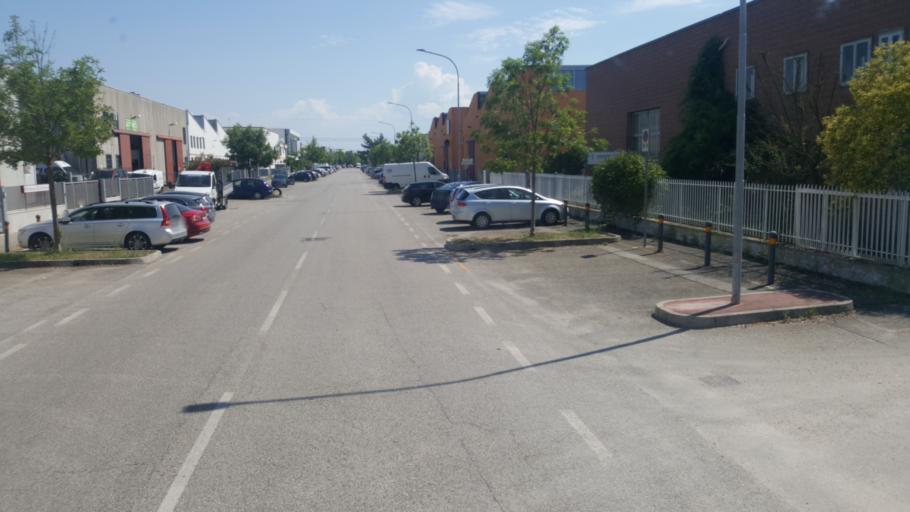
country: IT
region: Emilia-Romagna
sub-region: Provincia di Bologna
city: Castel Maggiore
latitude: 44.6070
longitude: 11.3643
